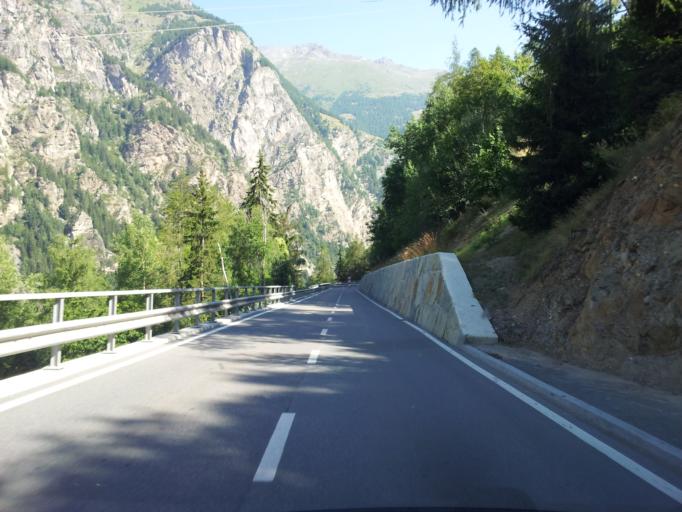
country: CH
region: Valais
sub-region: Visp District
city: Sankt Niklaus
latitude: 46.1861
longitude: 7.8169
